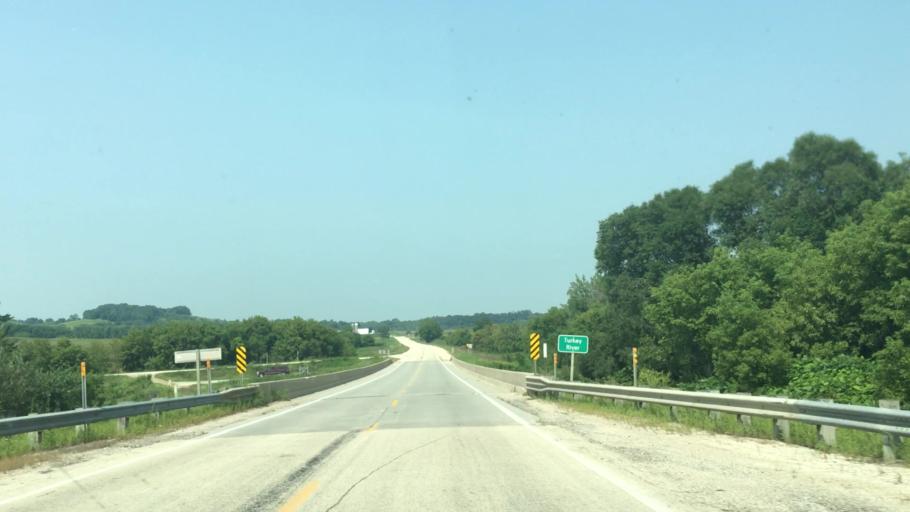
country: US
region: Iowa
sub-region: Fayette County
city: West Union
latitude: 43.0504
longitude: -91.8396
